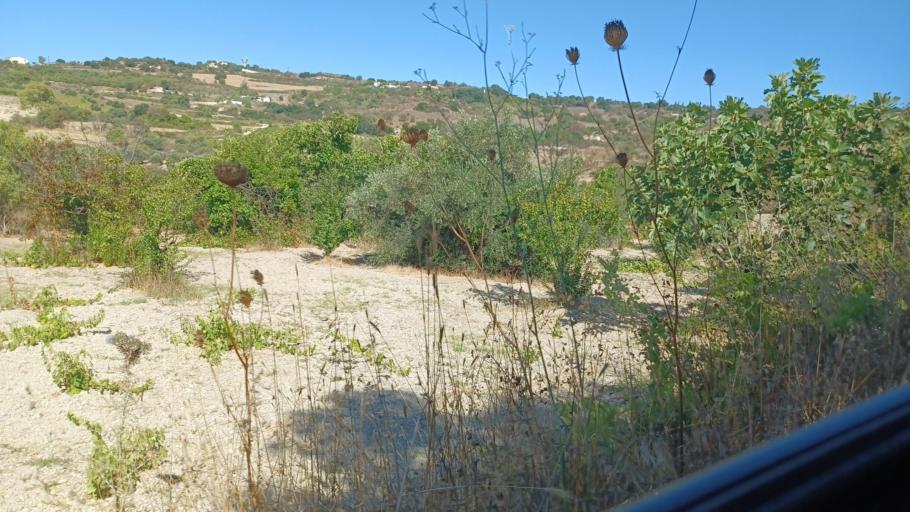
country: CY
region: Pafos
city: Mesogi
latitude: 34.8742
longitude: 32.5150
